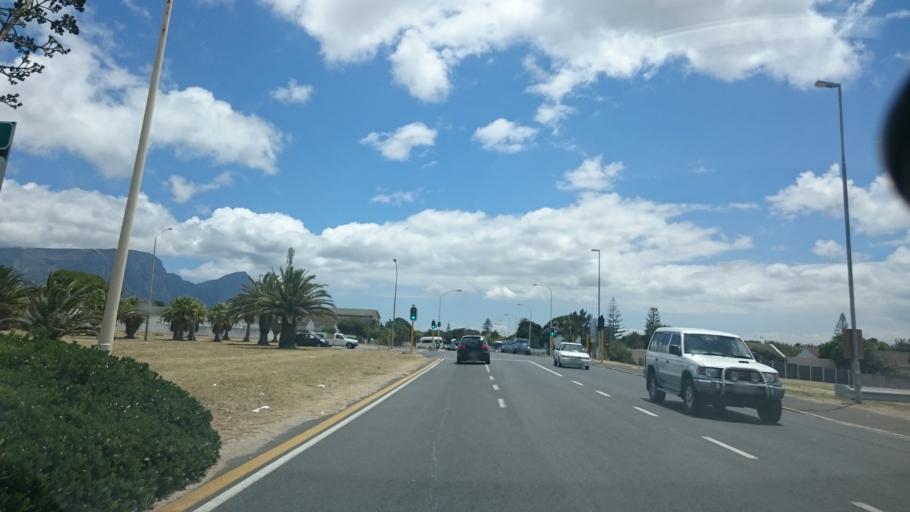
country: ZA
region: Western Cape
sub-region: City of Cape Town
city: Bergvliet
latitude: -34.0536
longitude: 18.4613
